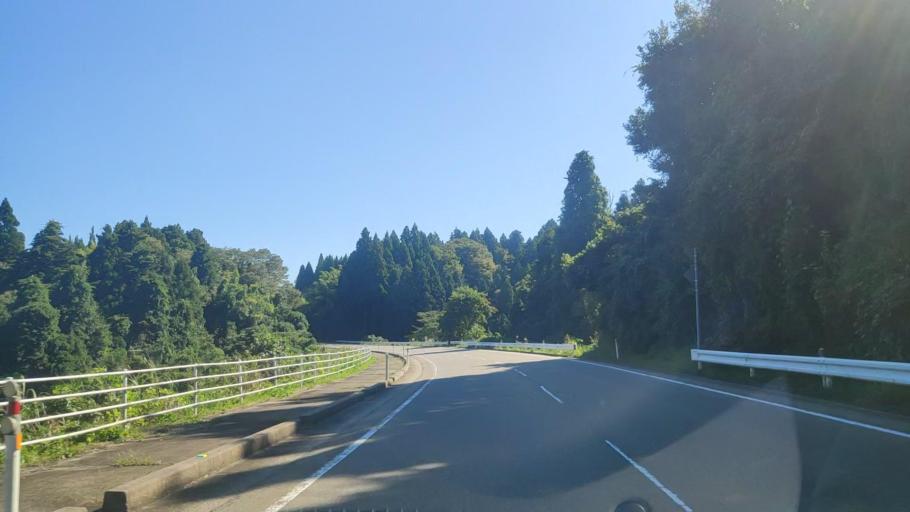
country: JP
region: Ishikawa
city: Nanao
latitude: 37.3782
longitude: 137.2335
